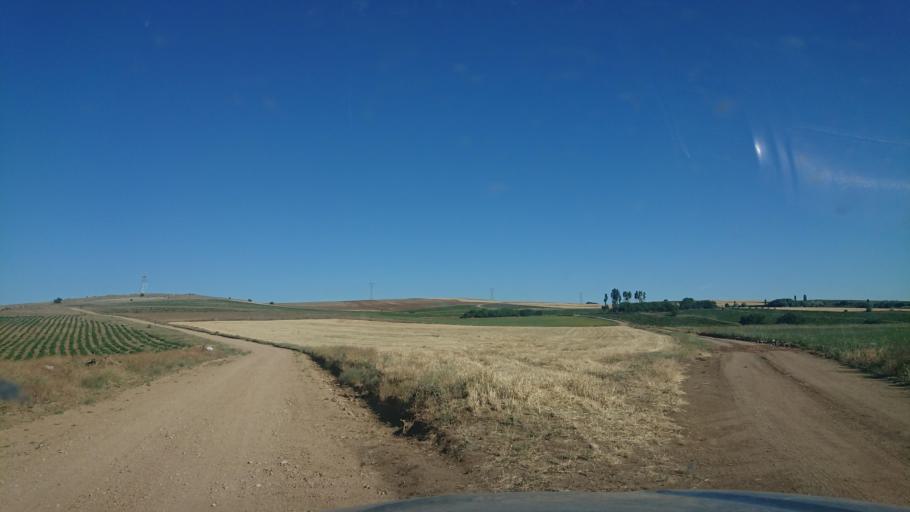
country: TR
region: Aksaray
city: Agacoren
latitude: 38.8279
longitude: 33.9537
